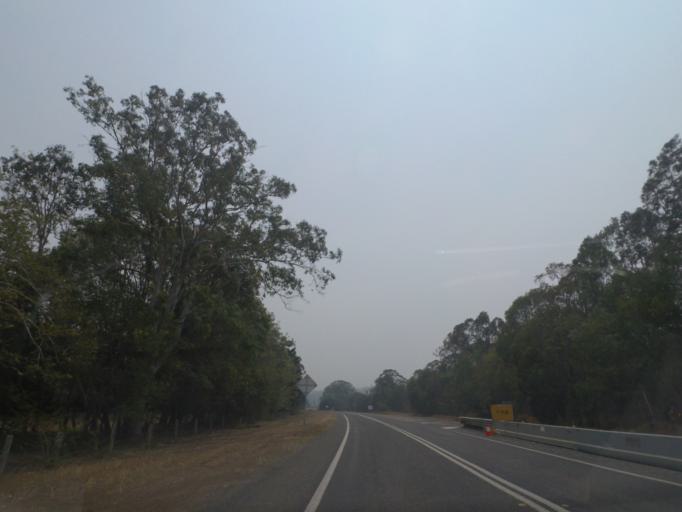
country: AU
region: New South Wales
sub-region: Clarence Valley
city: Maclean
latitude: -29.5486
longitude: 153.1560
